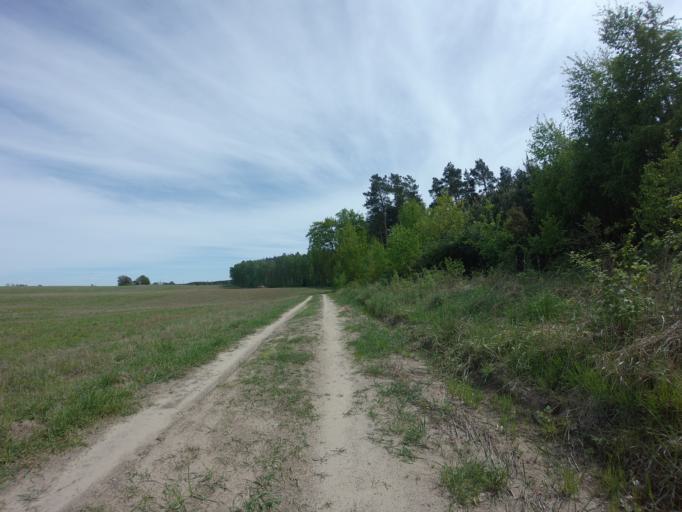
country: PL
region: West Pomeranian Voivodeship
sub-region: Powiat choszczenski
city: Recz
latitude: 53.1560
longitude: 15.5876
